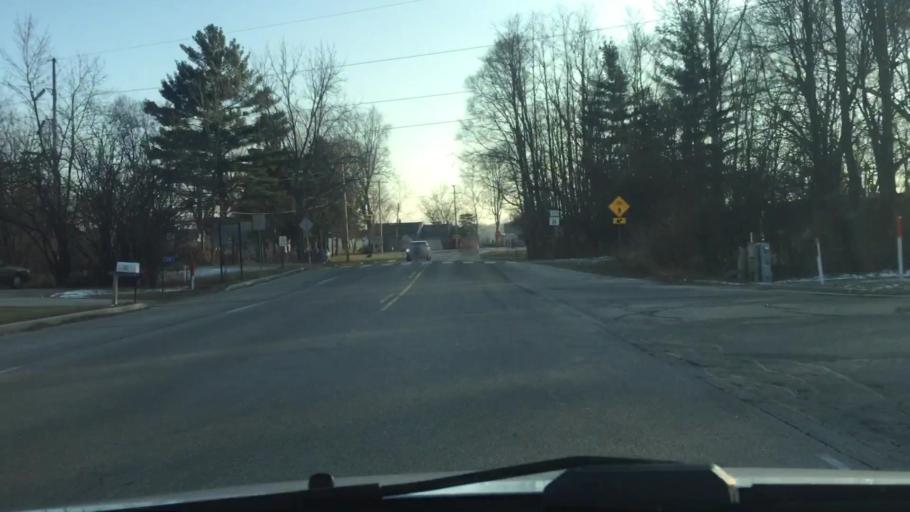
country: US
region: Wisconsin
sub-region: Waukesha County
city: Oconomowoc
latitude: 43.0832
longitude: -88.4956
